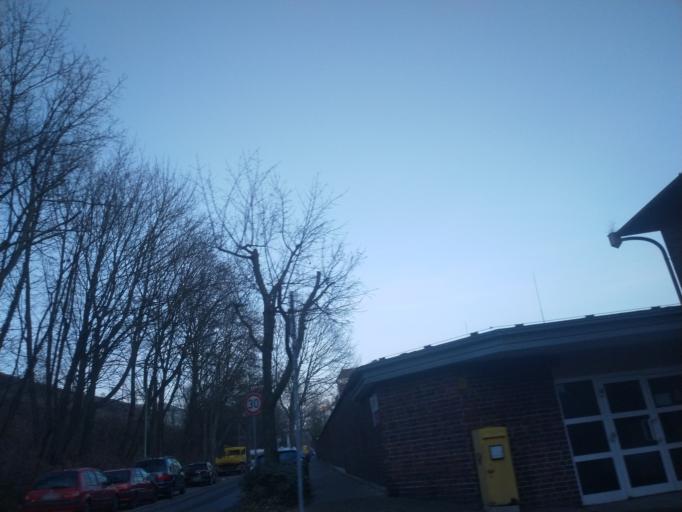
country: DE
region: Baden-Wuerttemberg
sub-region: Karlsruhe Region
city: Pforzheim
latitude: 48.8979
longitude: 8.7202
